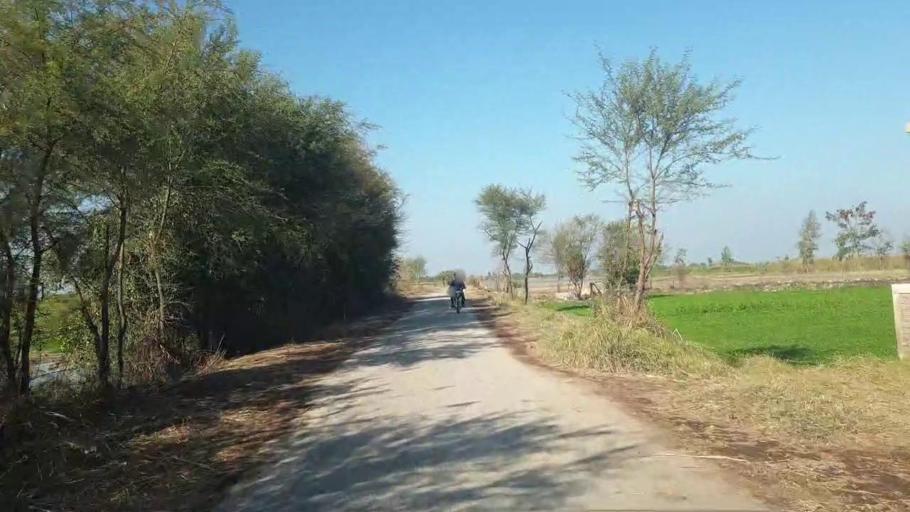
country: PK
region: Sindh
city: Shahdadpur
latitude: 25.9174
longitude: 68.5301
